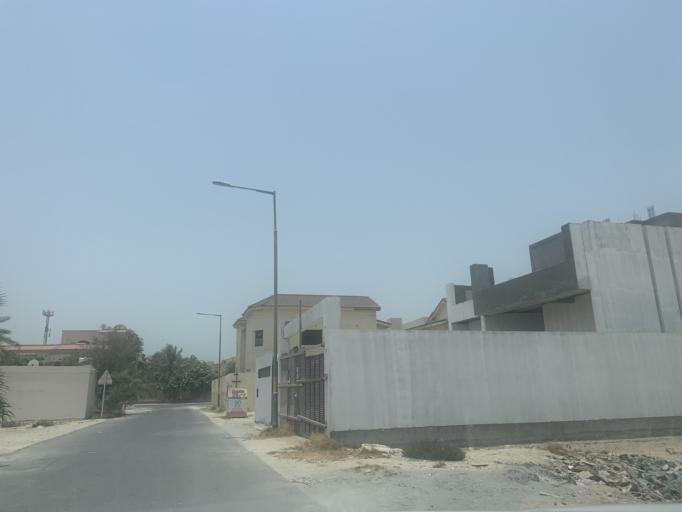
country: BH
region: Manama
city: Jidd Hafs
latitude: 26.2222
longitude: 50.4599
